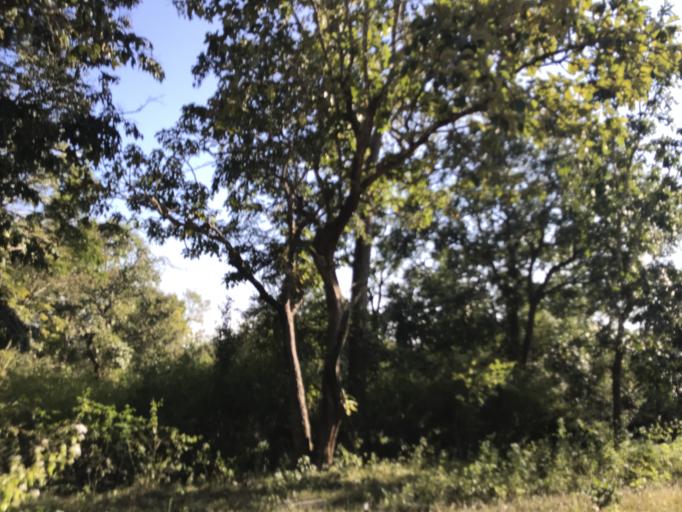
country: IN
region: Karnataka
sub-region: Mysore
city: Heggadadevankote
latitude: 11.9600
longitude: 76.2369
